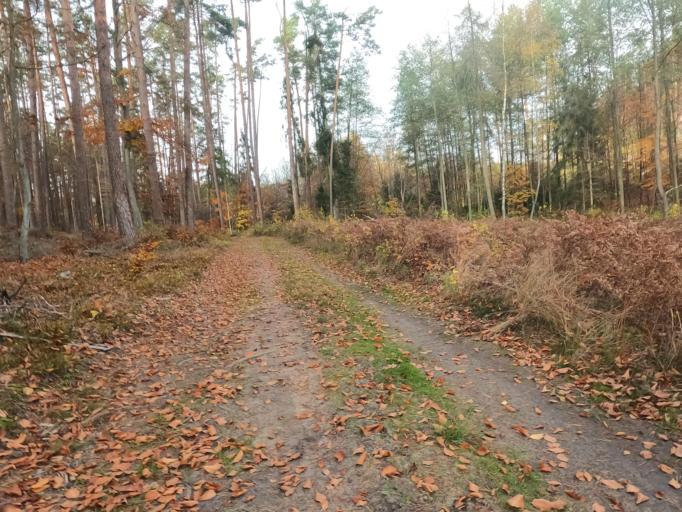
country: PL
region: Pomeranian Voivodeship
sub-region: Powiat starogardzki
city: Skarszewy
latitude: 54.0101
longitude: 18.4644
